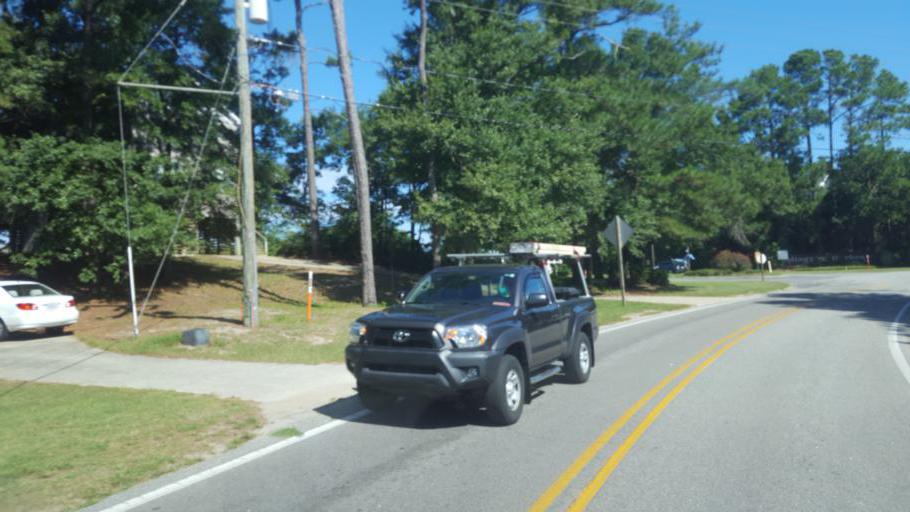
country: US
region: North Carolina
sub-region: Dare County
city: Kill Devil Hills
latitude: 36.0126
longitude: -75.7118
